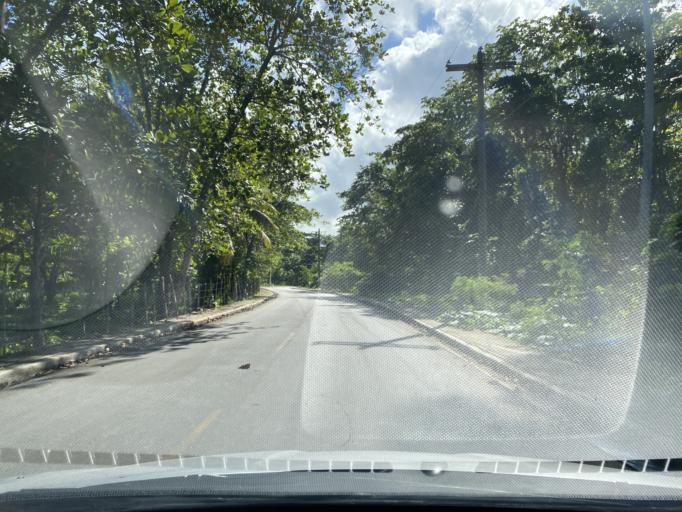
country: DO
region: Samana
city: Las Terrenas
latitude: 19.3219
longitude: -69.5293
